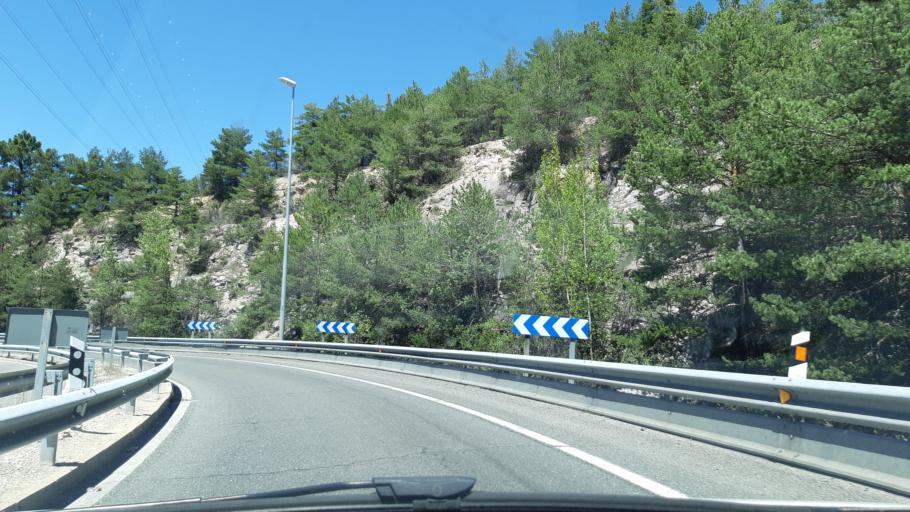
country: ES
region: Castille and Leon
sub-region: Provincia de Segovia
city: Otero de Herreros
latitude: 40.7288
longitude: -4.1920
